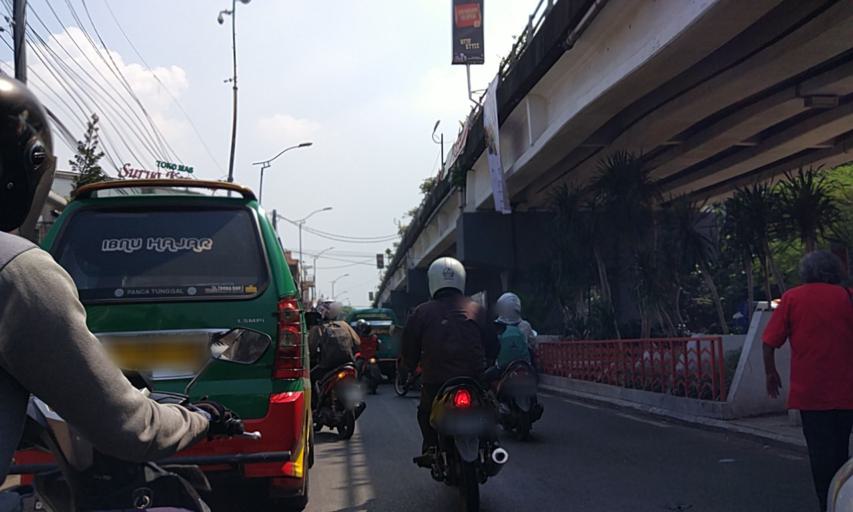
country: ID
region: West Java
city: Cimahi
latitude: -6.8968
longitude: 107.5607
